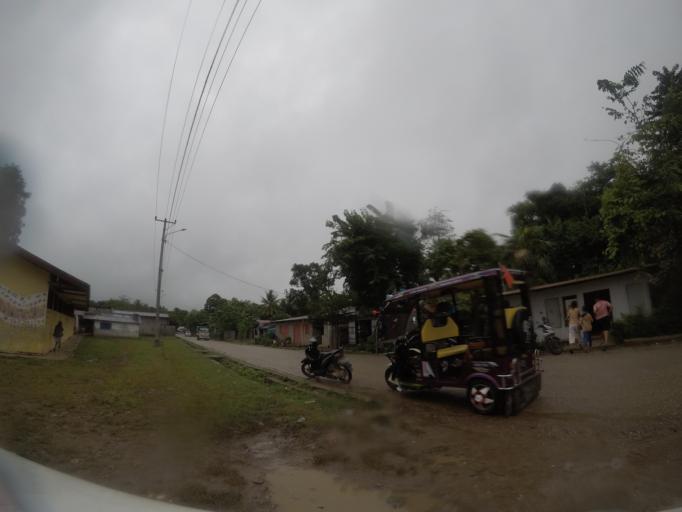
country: TL
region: Lautem
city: Lospalos
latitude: -8.5209
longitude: 126.9991
